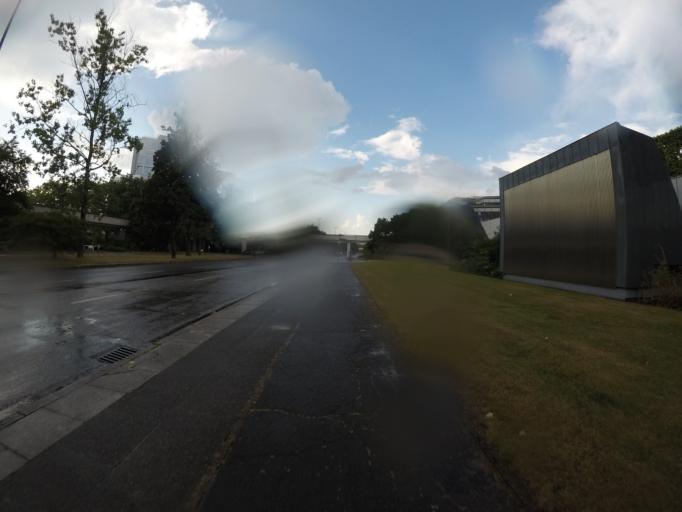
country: DE
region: Hamburg
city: Alsterdorf
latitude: 53.6017
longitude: 10.0175
